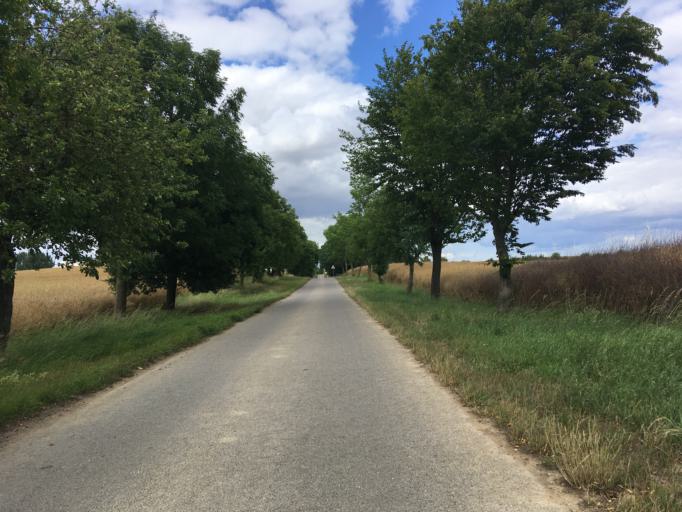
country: DE
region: Brandenburg
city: Gramzow
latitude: 53.2582
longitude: 14.0147
